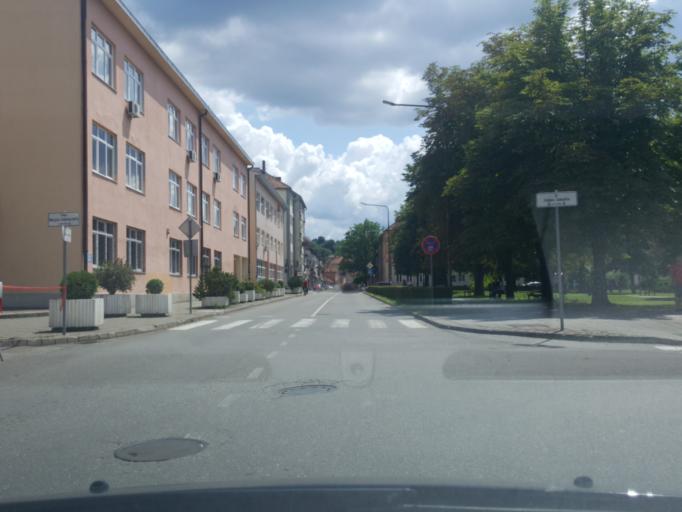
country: RS
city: Trsic
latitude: 44.5316
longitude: 19.2245
